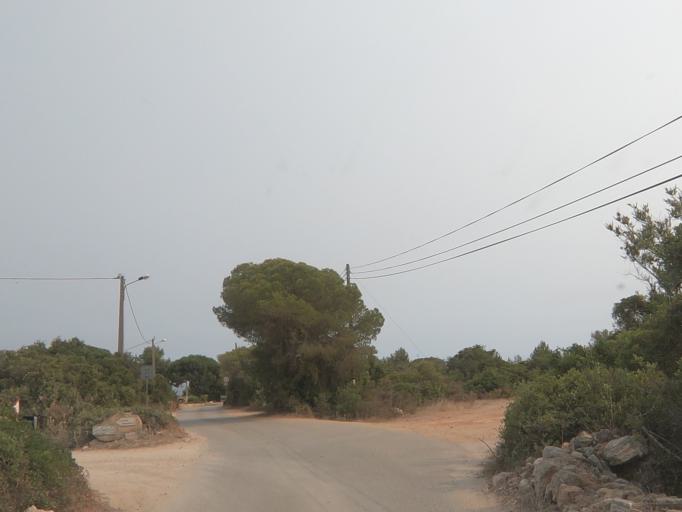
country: PT
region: Faro
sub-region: Silves
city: Armacao de Pera
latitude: 37.0951
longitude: -8.4028
